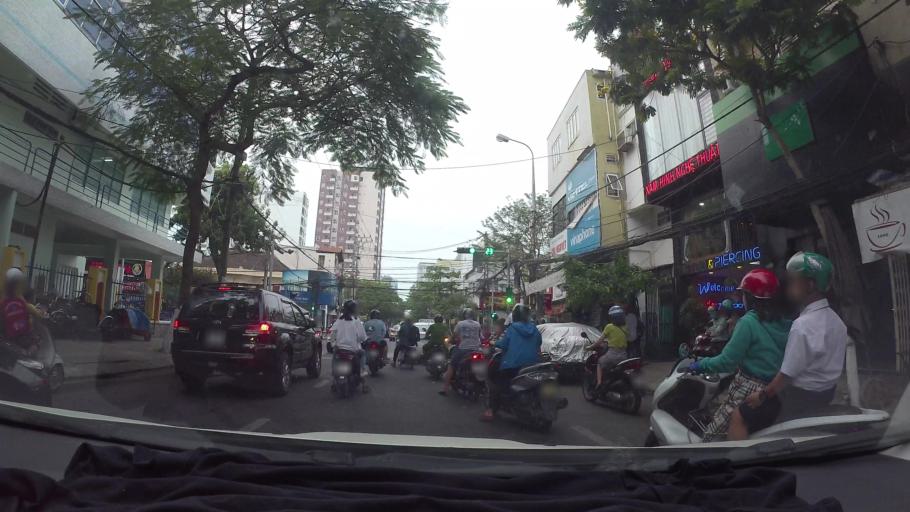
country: VN
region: Da Nang
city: Da Nang
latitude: 16.0746
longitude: 108.2207
